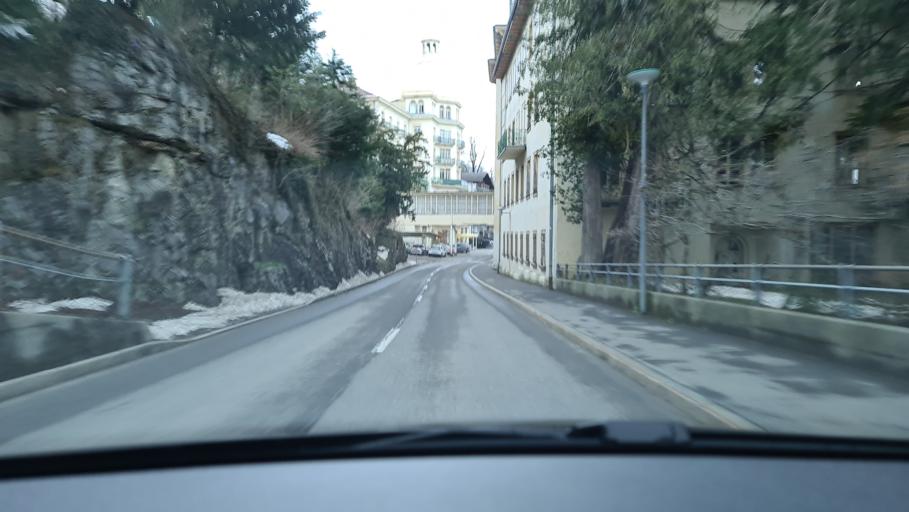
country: CH
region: Uri
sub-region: Uri
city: Bauen
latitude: 46.9691
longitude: 8.5860
